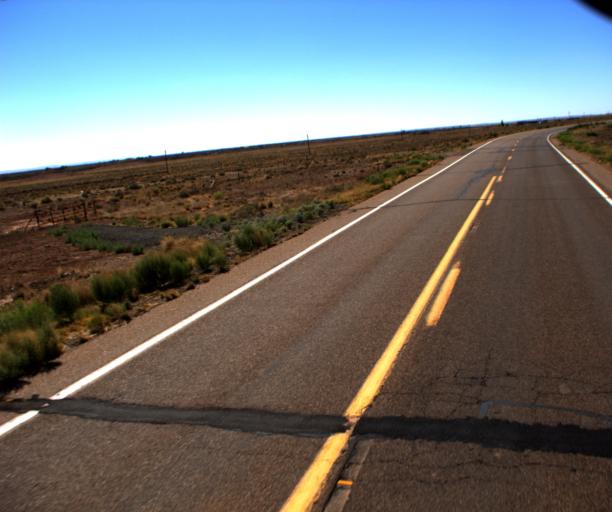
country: US
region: Arizona
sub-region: Coconino County
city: LeChee
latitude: 35.2901
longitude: -110.9861
